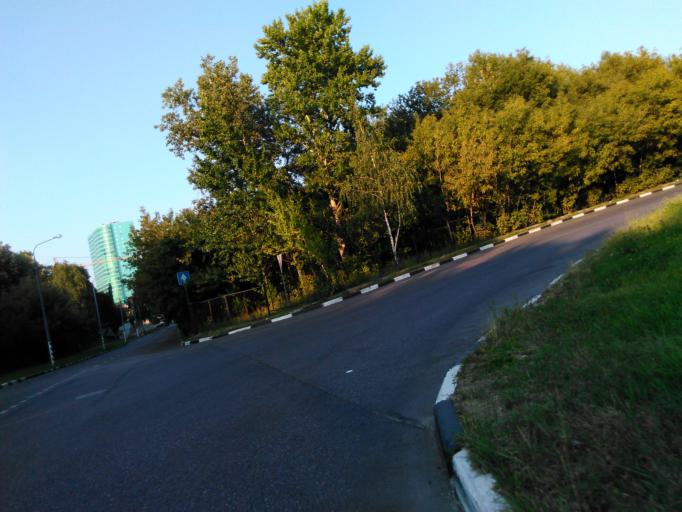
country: RU
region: Moskovskaya
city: Cheremushki
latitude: 55.6580
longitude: 37.5482
